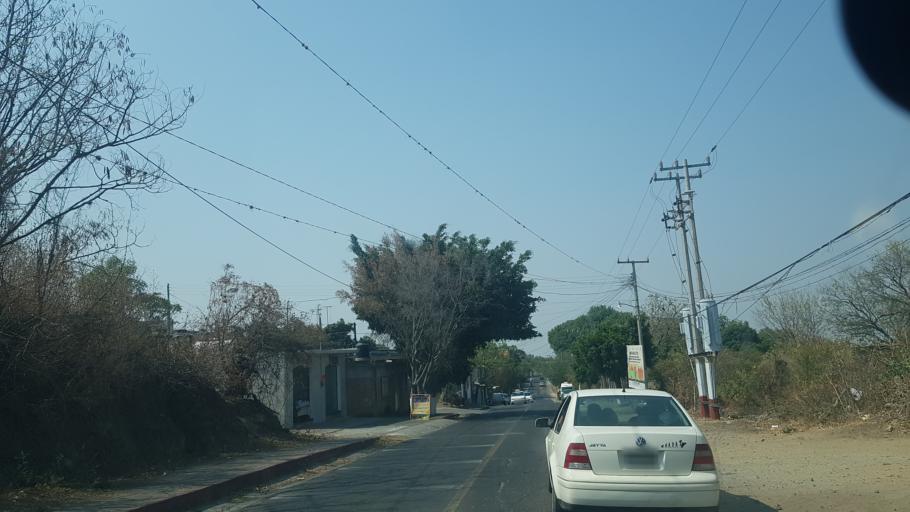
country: MX
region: Morelos
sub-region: Zacualpan
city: Zacualpan de Amilpas
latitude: 18.7811
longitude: -98.7732
